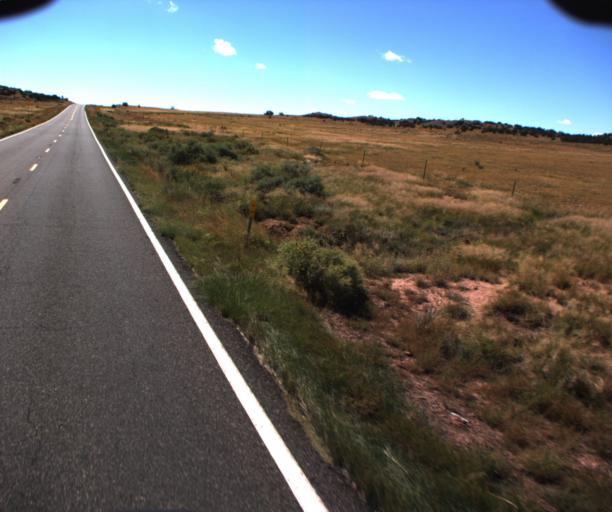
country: US
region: Arizona
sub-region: Apache County
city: Saint Johns
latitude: 34.7612
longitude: -109.2424
